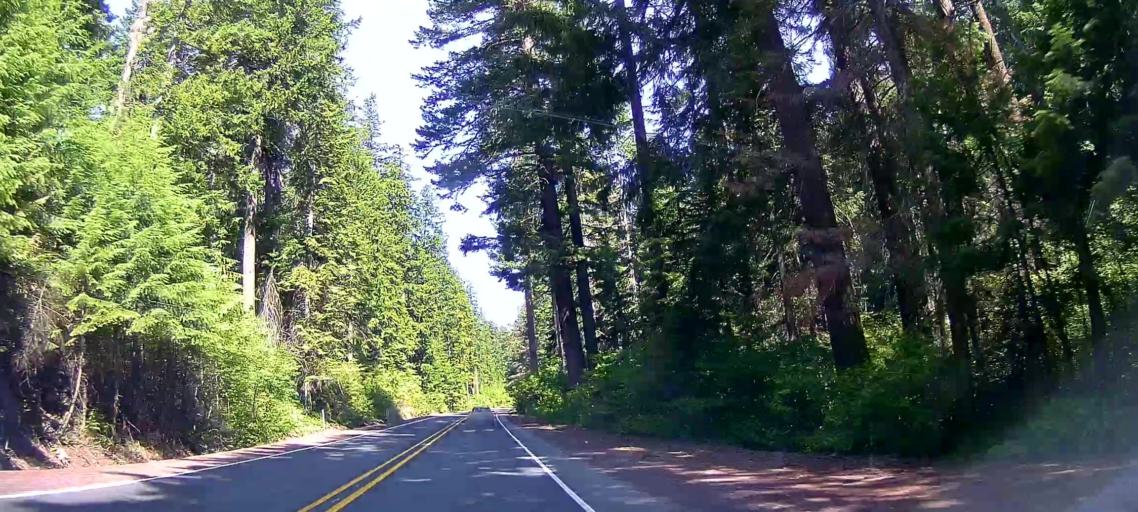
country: US
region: Oregon
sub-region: Jefferson County
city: Warm Springs
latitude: 45.1084
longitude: -121.5606
